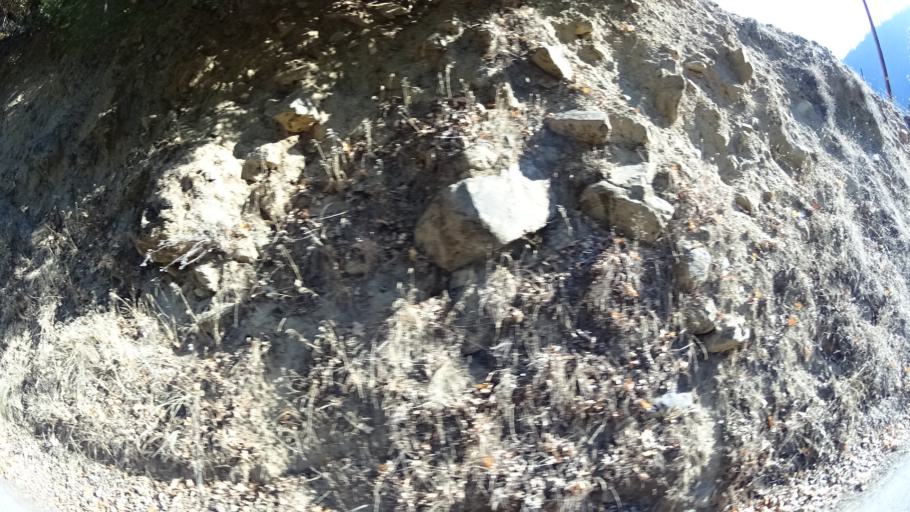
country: US
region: California
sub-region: Siskiyou County
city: Happy Camp
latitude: 41.6923
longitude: -123.0713
